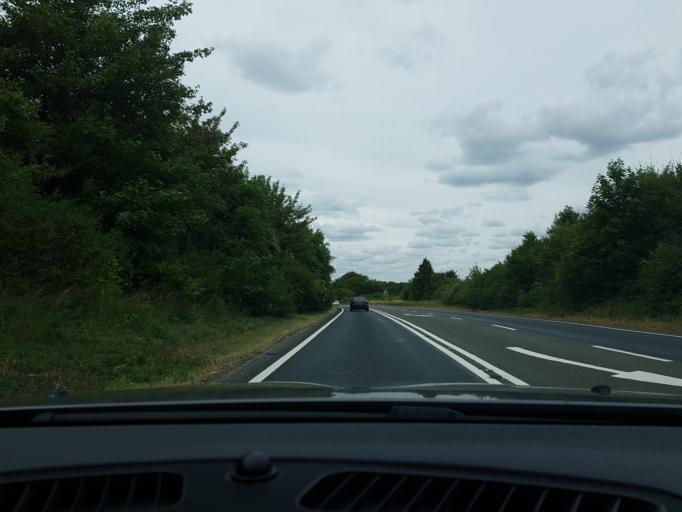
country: GB
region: England
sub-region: Hampshire
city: Kingsclere
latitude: 51.3126
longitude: -1.2011
